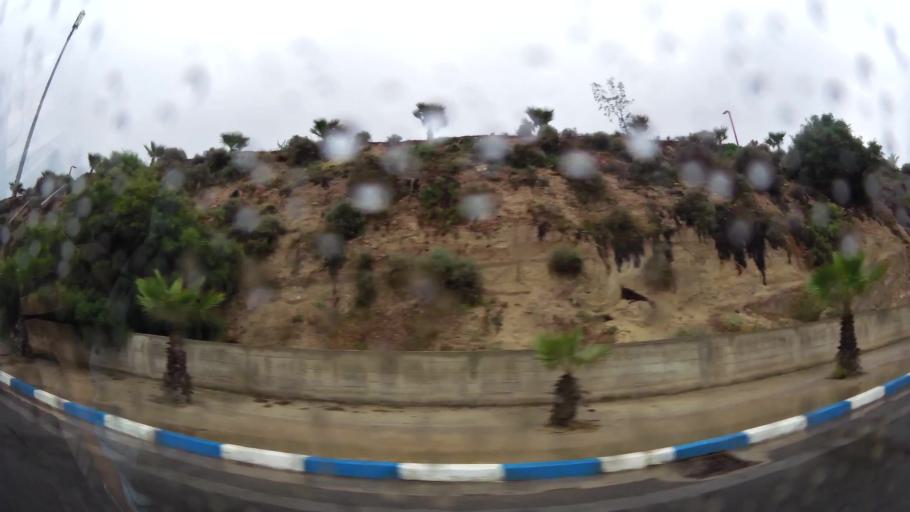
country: MA
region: Taza-Al Hoceima-Taounate
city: Tirhanimine
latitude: 35.2464
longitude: -3.9543
